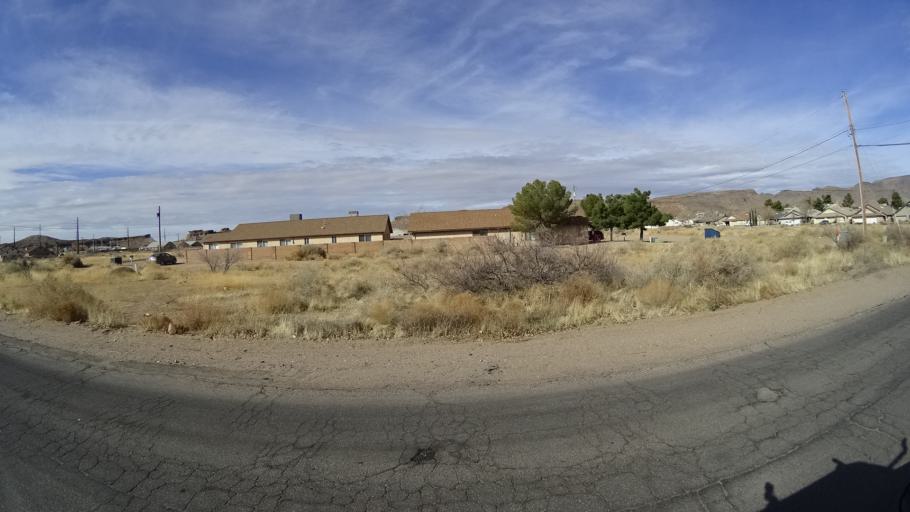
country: US
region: Arizona
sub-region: Mohave County
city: Kingman
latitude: 35.2197
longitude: -114.0401
